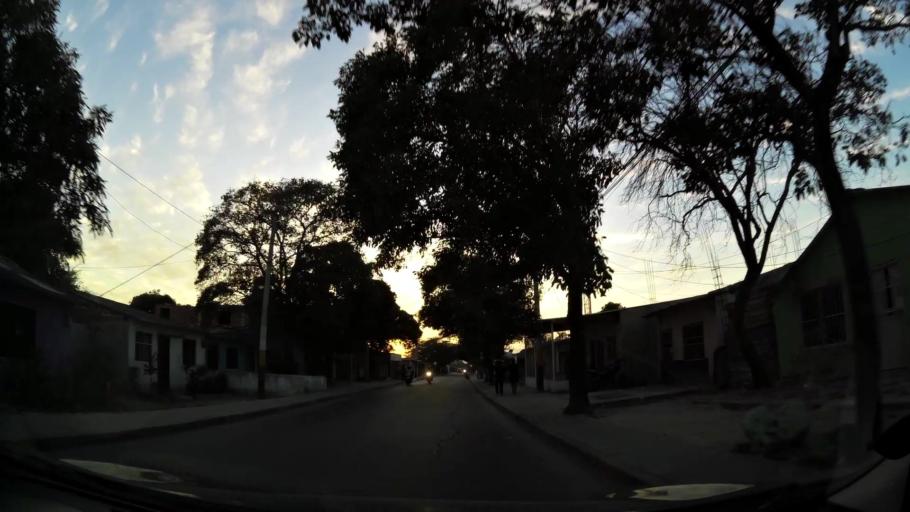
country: CO
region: Atlantico
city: Barranquilla
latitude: 10.9585
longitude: -74.8234
